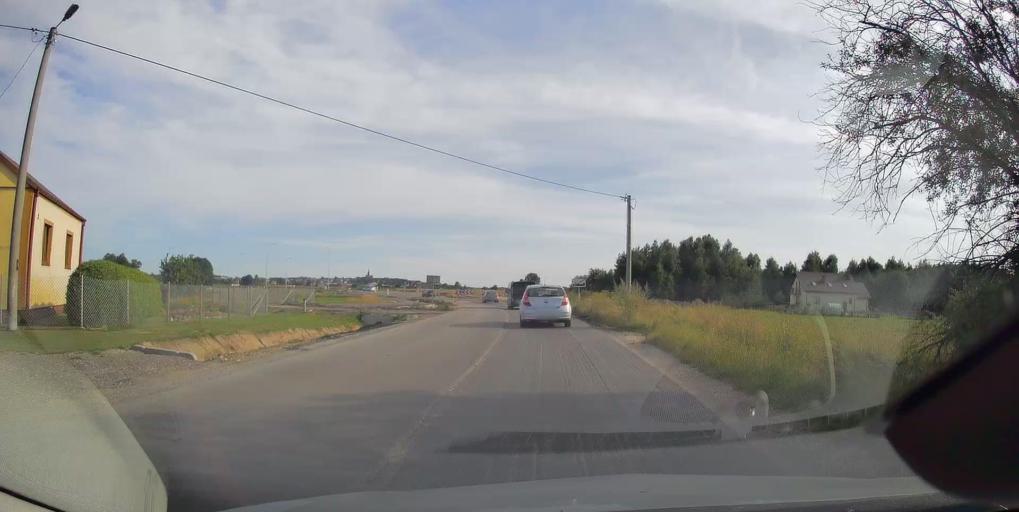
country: PL
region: Swietokrzyskie
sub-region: Powiat kielecki
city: Lopuszno
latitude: 50.9679
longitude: 20.2452
